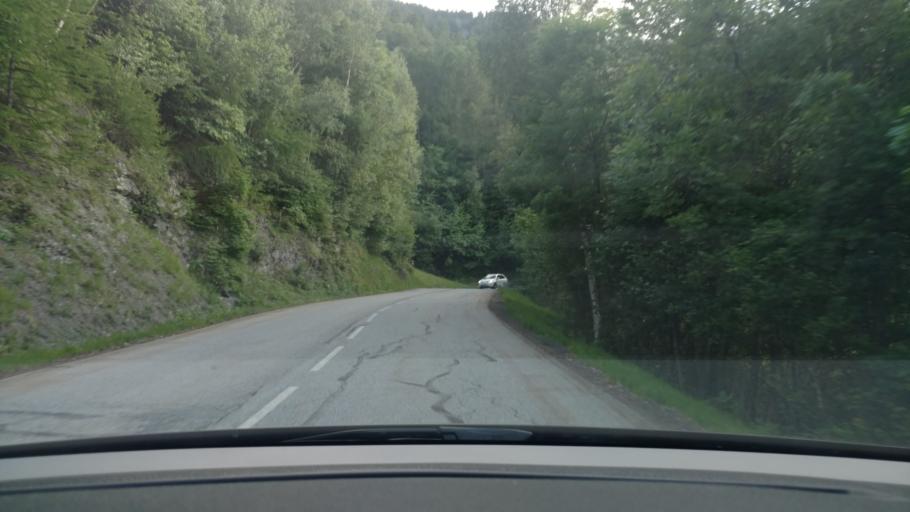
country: FR
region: Rhone-Alpes
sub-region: Departement de la Savoie
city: Villargondran
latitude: 45.2406
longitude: 6.4097
